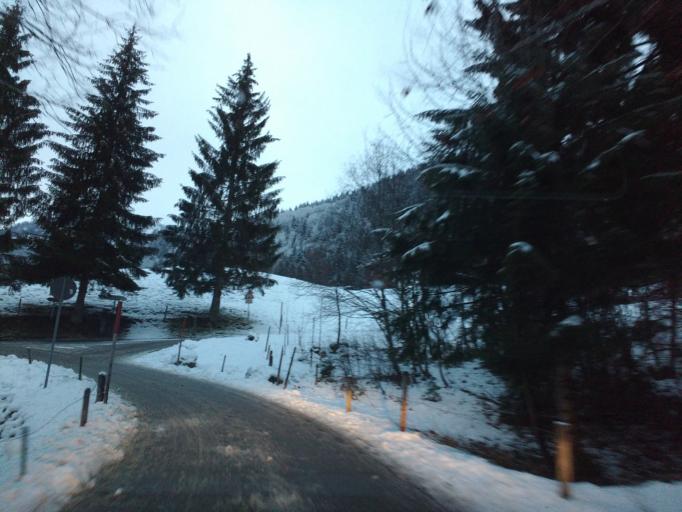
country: DE
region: Bavaria
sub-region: Swabia
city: Obermaiselstein
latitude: 47.4018
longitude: 10.2218
